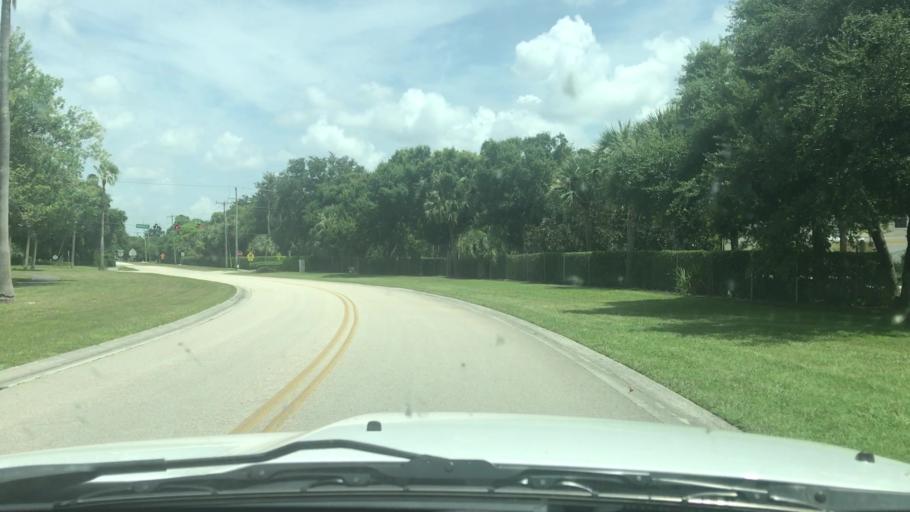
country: US
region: Florida
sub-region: Indian River County
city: Florida Ridge
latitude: 27.5620
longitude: -80.3812
